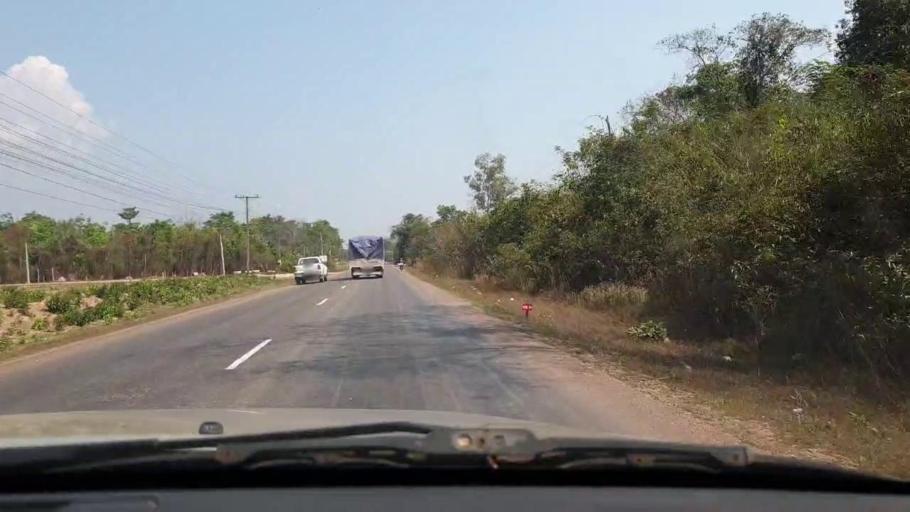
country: TH
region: Nong Khai
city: Phon Phisai
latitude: 18.1502
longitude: 103.0552
